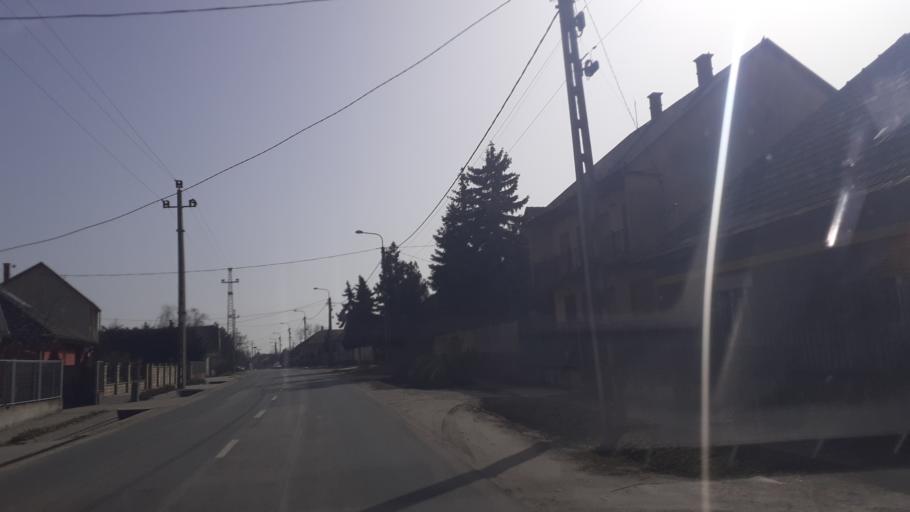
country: HU
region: Pest
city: Bugyi
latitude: 47.2238
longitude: 19.1435
